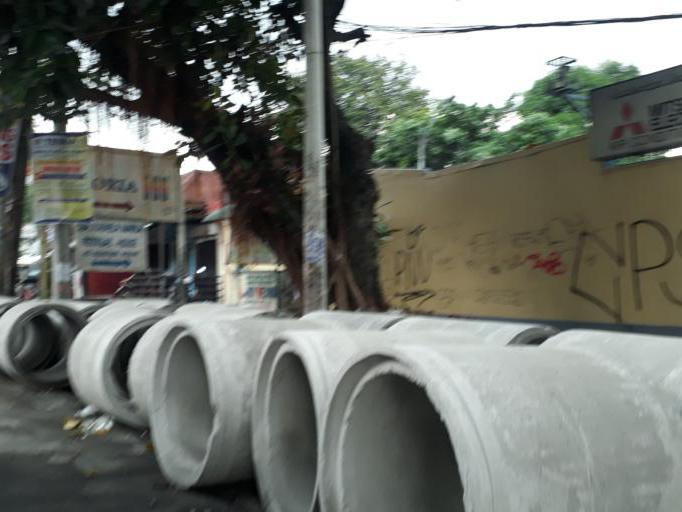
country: PH
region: Metro Manila
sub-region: Quezon City
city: Quezon City
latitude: 14.6694
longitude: 121.0538
